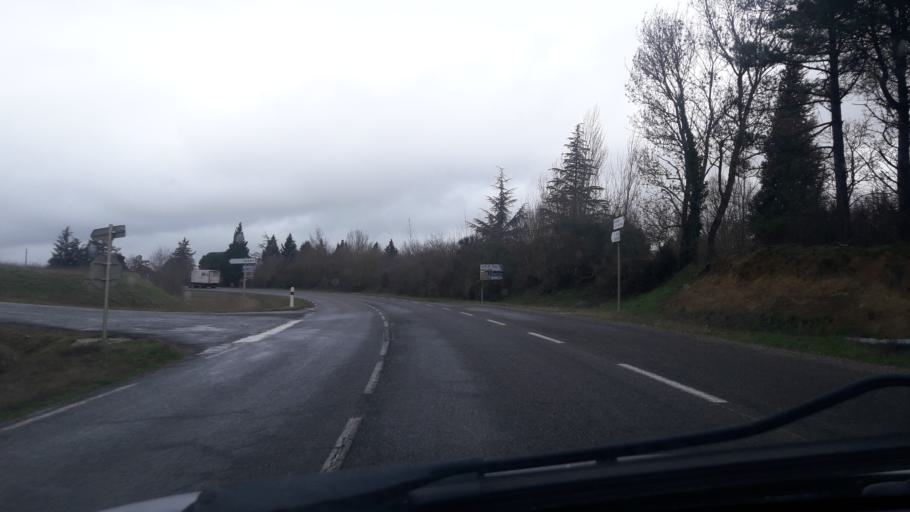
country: FR
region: Midi-Pyrenees
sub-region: Departement du Gers
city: Gimont
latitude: 43.6842
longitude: 1.0044
